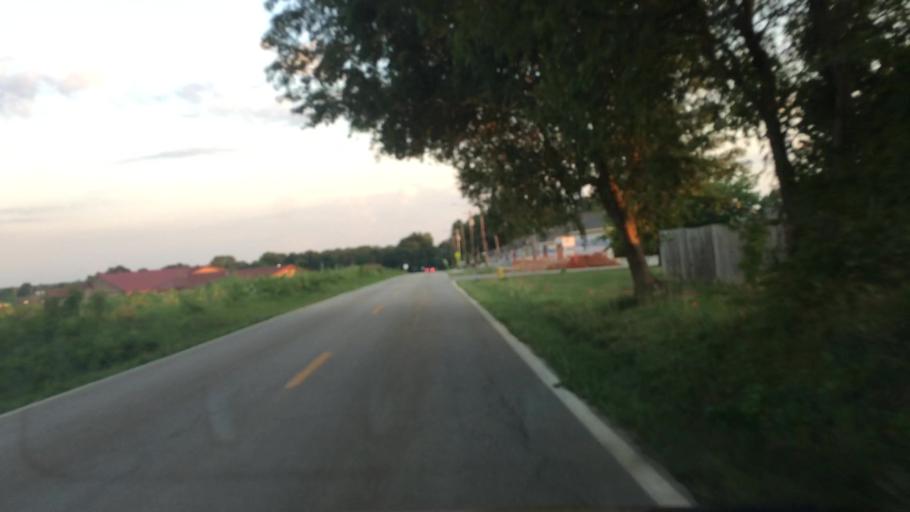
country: US
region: Missouri
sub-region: Greene County
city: Springfield
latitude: 37.2020
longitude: -93.3743
